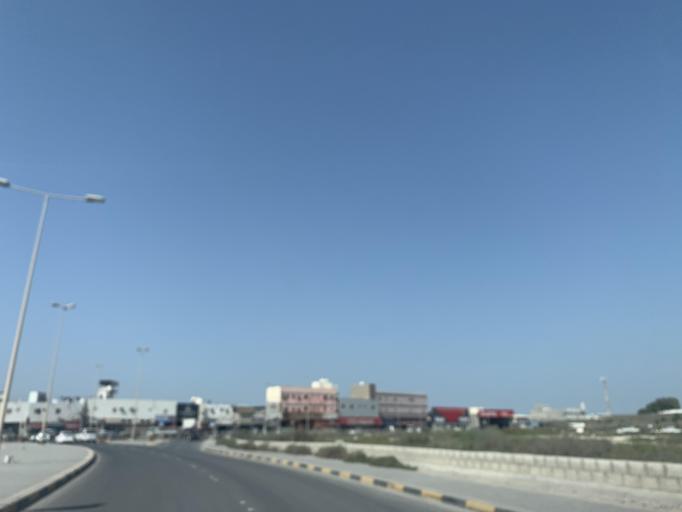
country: BH
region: Central Governorate
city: Madinat Hamad
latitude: 26.1386
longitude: 50.4890
